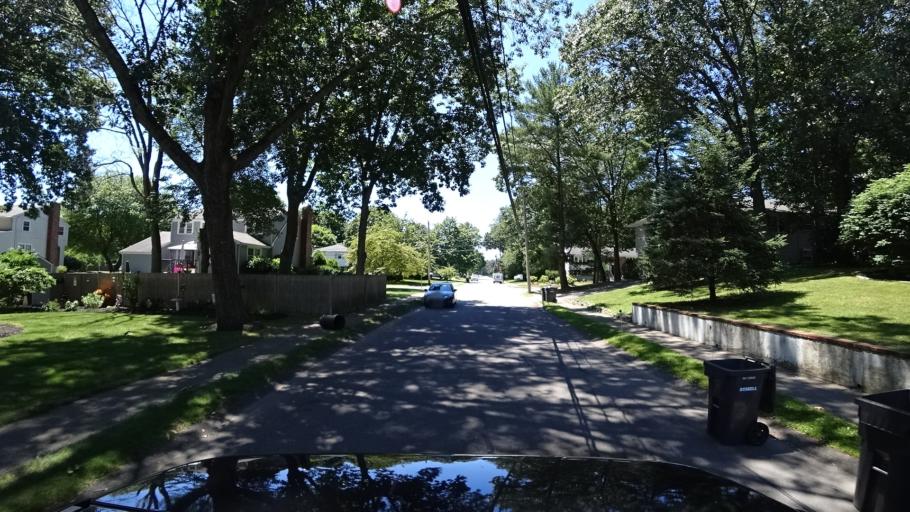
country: US
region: Massachusetts
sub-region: Norfolk County
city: Dedham
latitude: 42.2237
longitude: -71.1512
